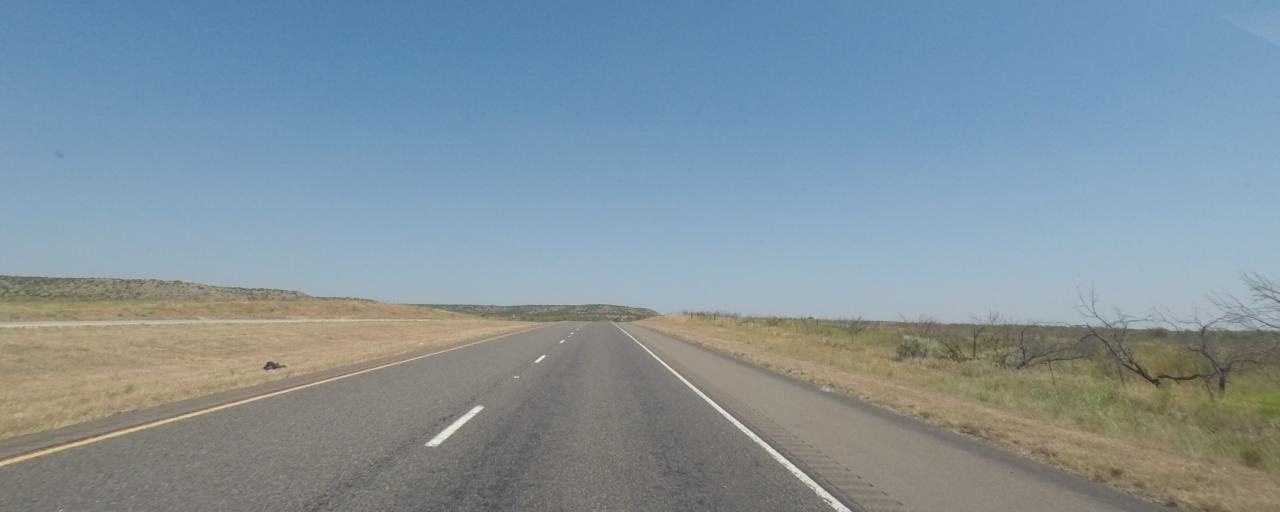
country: US
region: Texas
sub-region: Dickens County
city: Dickens
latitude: 33.6348
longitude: -100.8892
